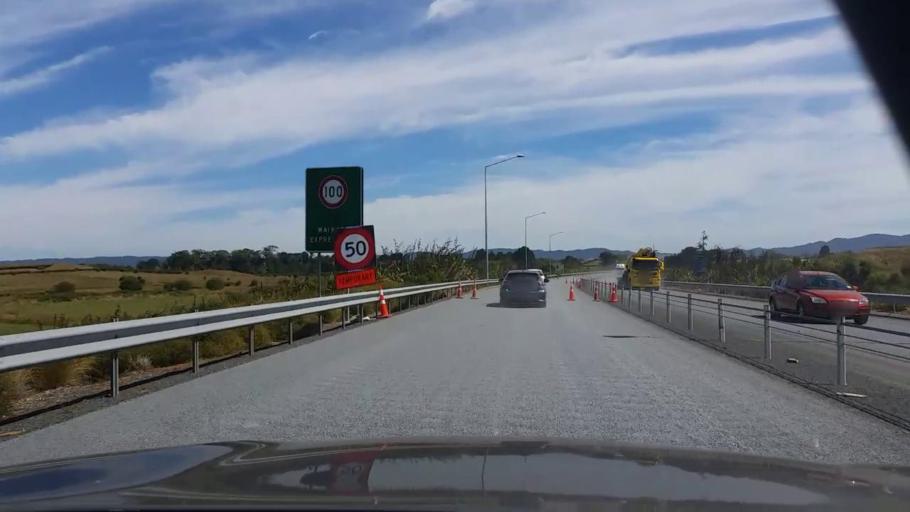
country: NZ
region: Waikato
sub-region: Hamilton City
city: Hamilton
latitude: -37.7531
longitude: 175.2226
